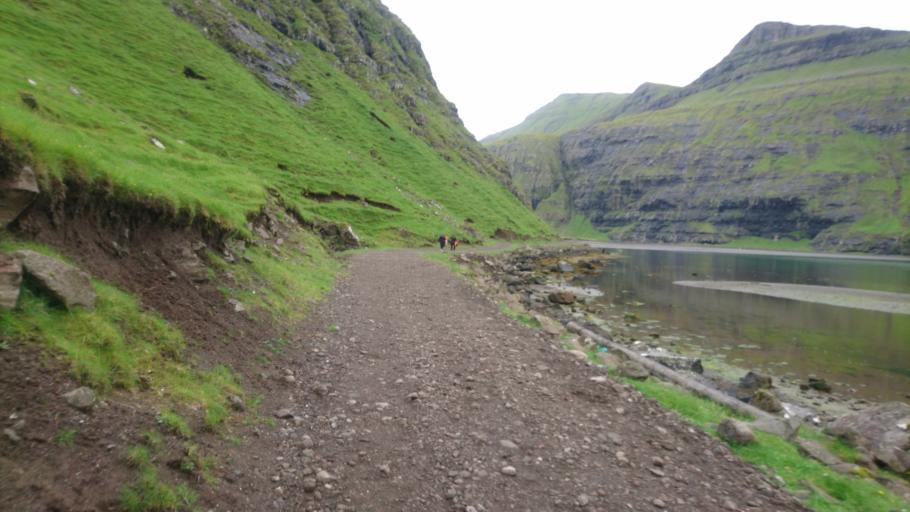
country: FO
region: Streymoy
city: Vestmanna
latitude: 62.2458
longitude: -7.1871
